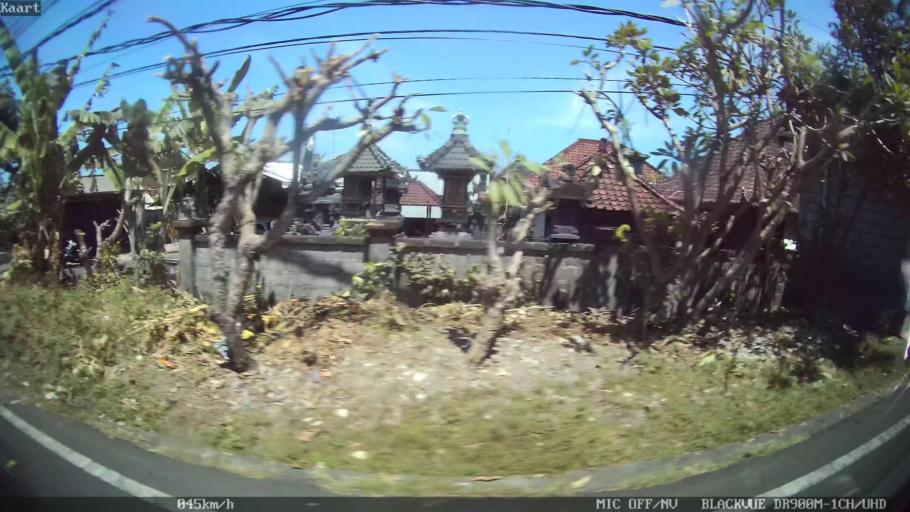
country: ID
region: Bali
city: Klungkung
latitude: -8.5777
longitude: 115.3524
